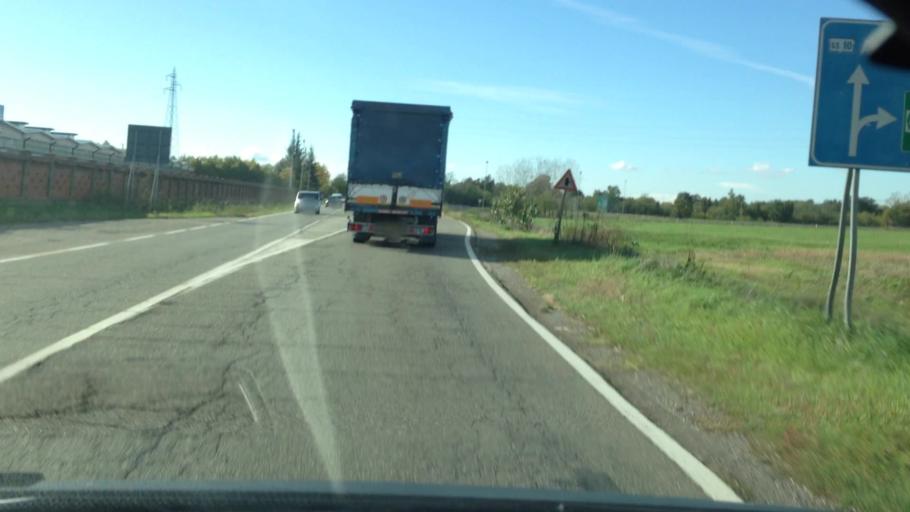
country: IT
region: Piedmont
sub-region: Provincia di Alessandria
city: Felizzano
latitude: 44.8999
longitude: 8.4235
